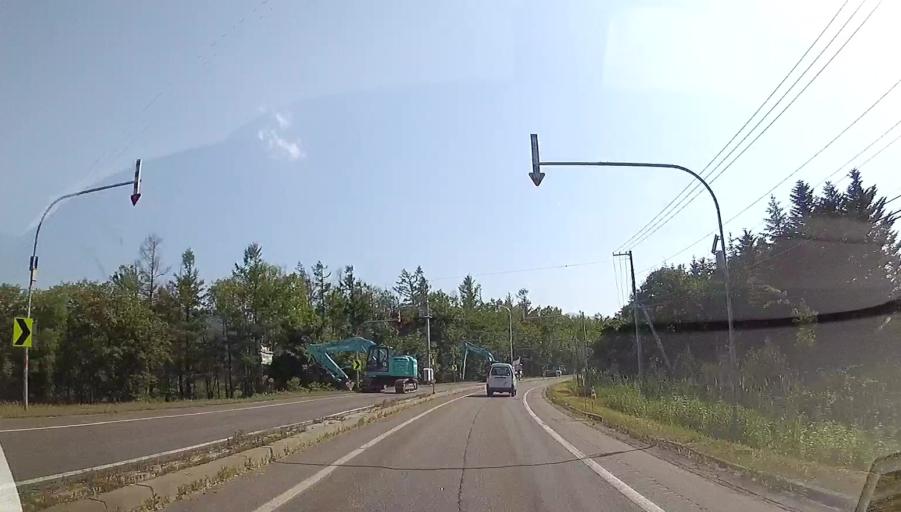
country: JP
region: Hokkaido
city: Otofuke
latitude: 42.9834
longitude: 142.8377
